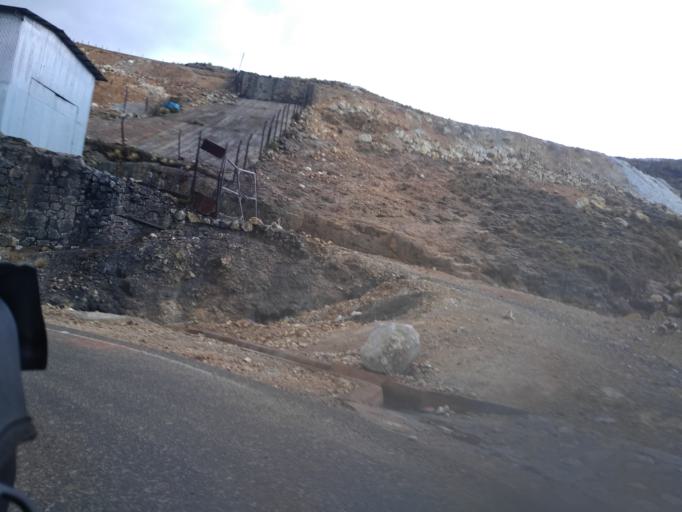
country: PE
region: La Libertad
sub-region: Provincia de Santiago de Chuco
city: Quiruvilca
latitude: -7.9973
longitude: -78.3076
